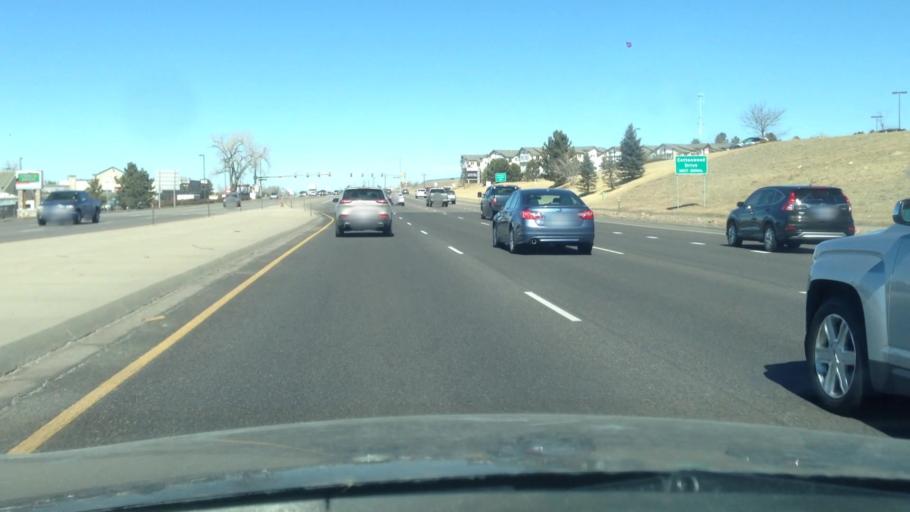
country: US
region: Colorado
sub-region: Douglas County
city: Stonegate
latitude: 39.5559
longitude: -104.7785
